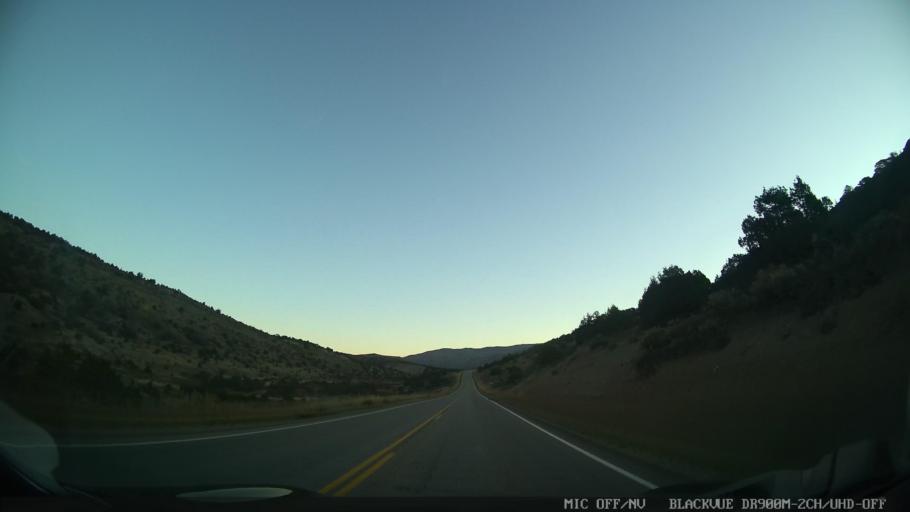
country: US
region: Colorado
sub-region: Eagle County
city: Edwards
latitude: 39.7141
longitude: -106.6838
